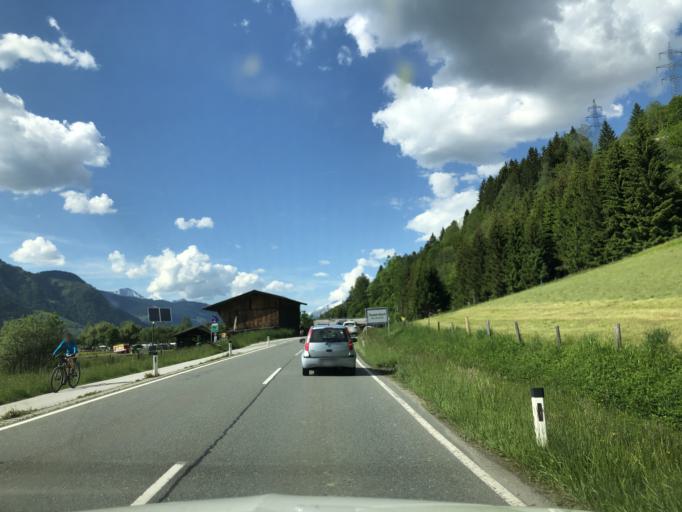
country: AT
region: Salzburg
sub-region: Politischer Bezirk Zell am See
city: Bruck an der Grossglocknerstrasse
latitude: 47.2994
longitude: 12.8158
